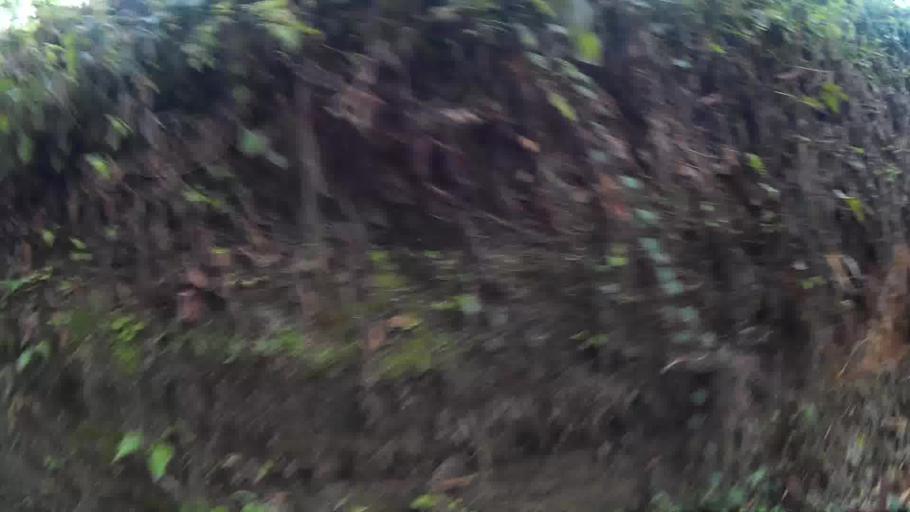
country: CO
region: Valle del Cauca
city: Ulloa
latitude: 4.7140
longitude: -75.7071
